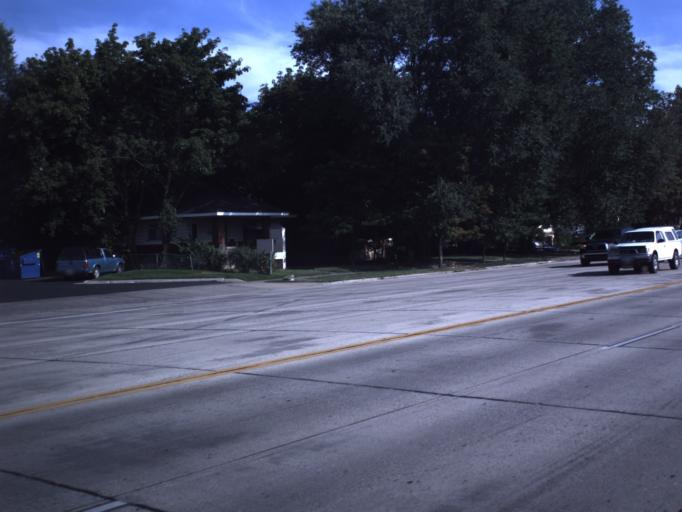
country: US
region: Utah
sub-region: Weber County
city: Ogden
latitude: 41.2514
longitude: -111.9699
